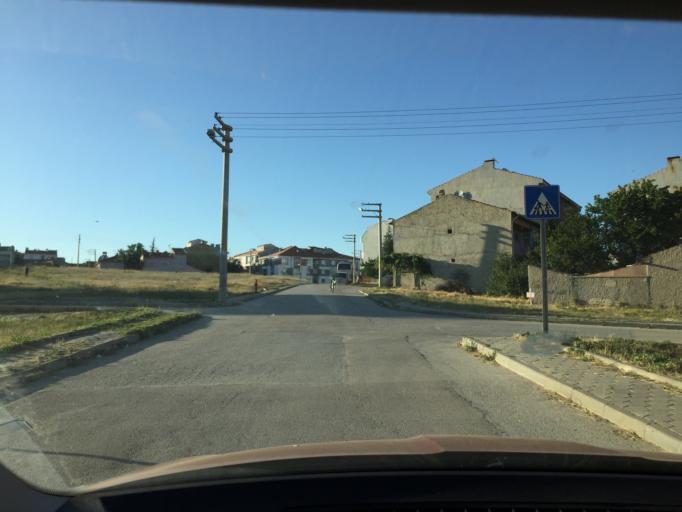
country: TR
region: Eskisehir
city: Eskisehir
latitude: 39.7769
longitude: 30.4529
